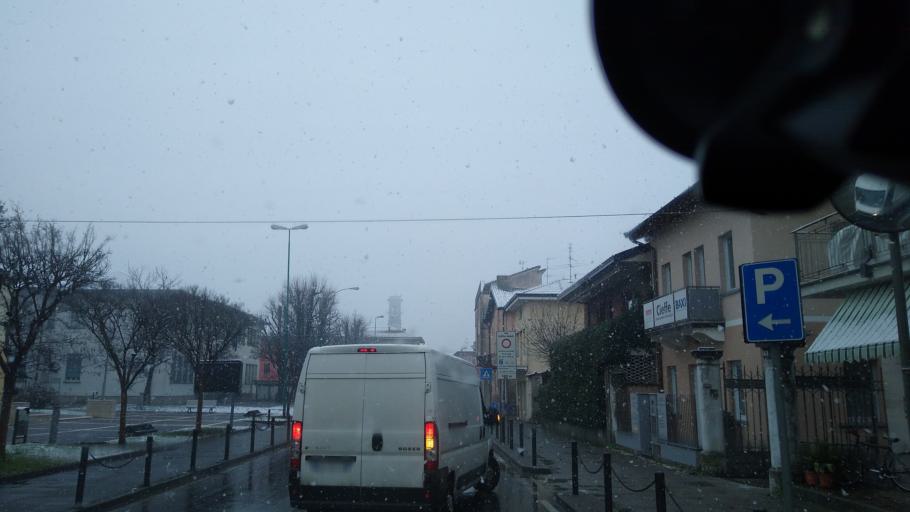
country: IT
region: Lombardy
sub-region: Provincia di Bergamo
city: Bariano
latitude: 45.5138
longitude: 9.7048
